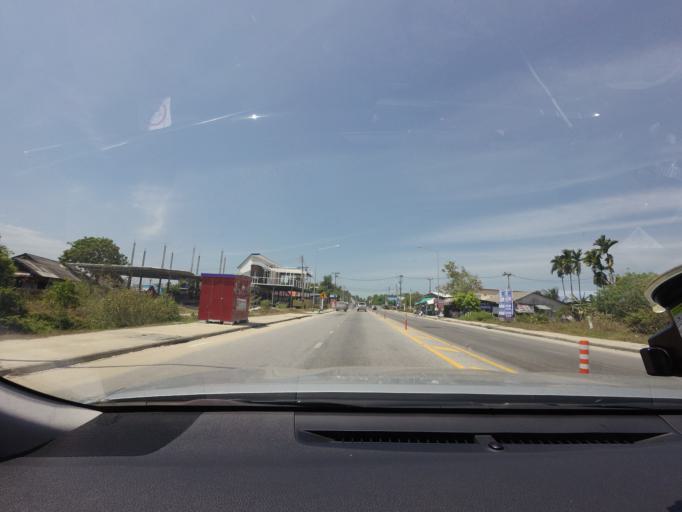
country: TH
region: Narathiwat
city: Narathiwat
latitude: 6.4304
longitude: 101.8155
